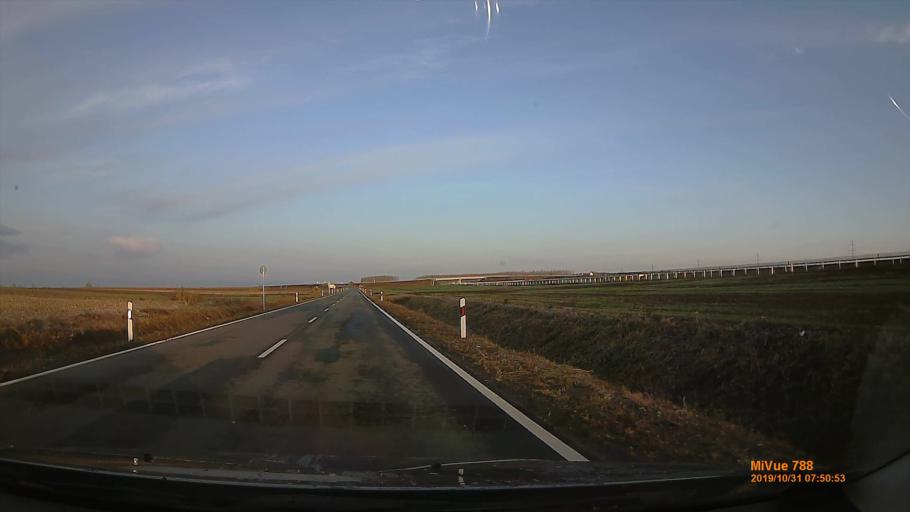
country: HU
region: Pest
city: Pilis
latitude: 47.3054
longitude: 19.5611
